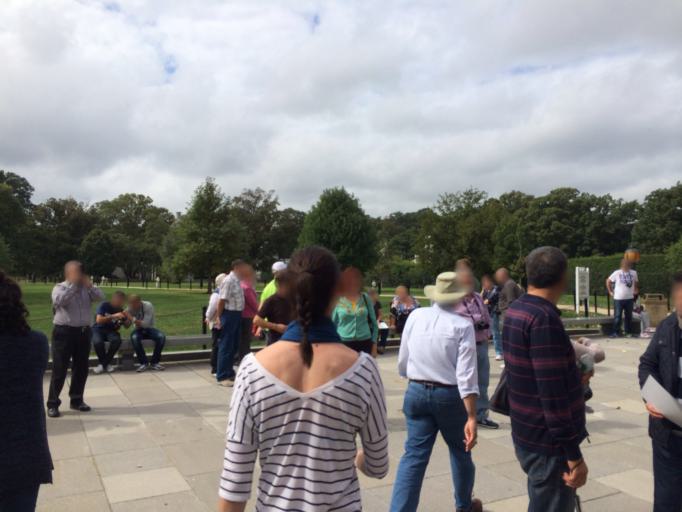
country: US
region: Washington, D.C.
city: Washington, D.C.
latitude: 38.8830
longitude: -77.0659
